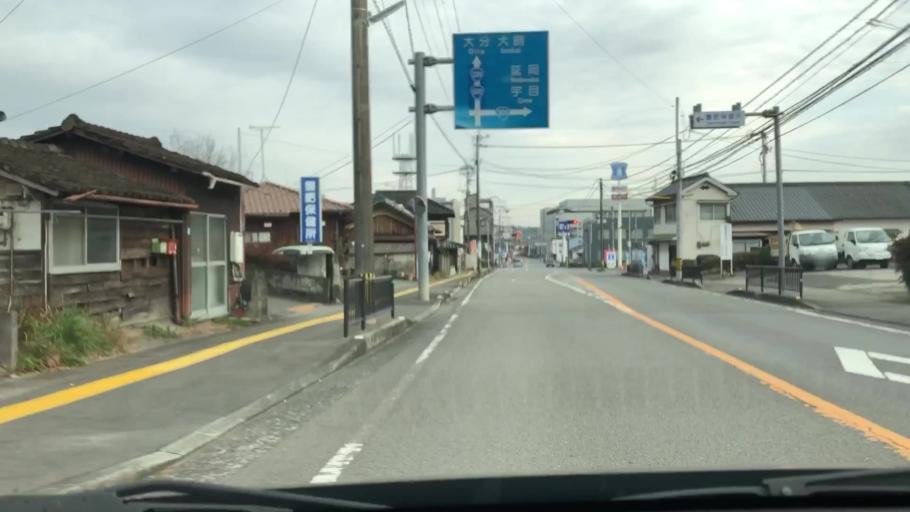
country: JP
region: Oita
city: Takedamachi
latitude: 32.9752
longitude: 131.5812
